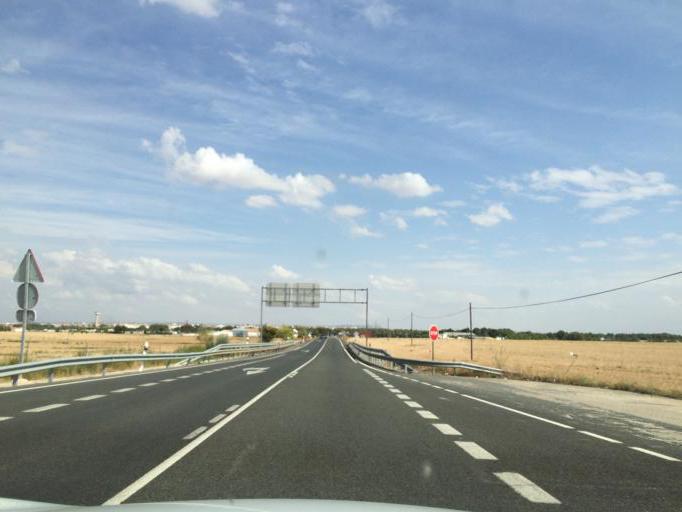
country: ES
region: Castille-La Mancha
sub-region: Provincia de Albacete
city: Albacete
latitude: 39.0006
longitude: -1.9007
